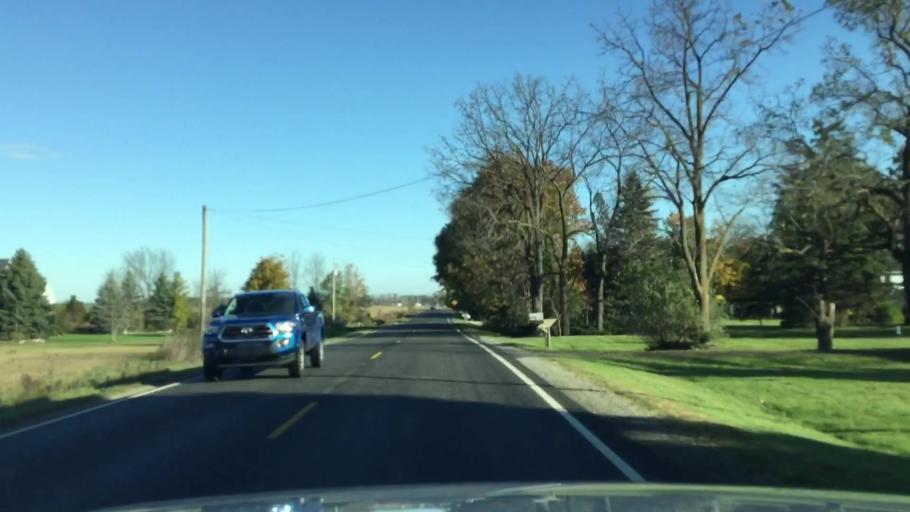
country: US
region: Michigan
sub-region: Shiawassee County
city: Durand
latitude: 42.9067
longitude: -83.9482
